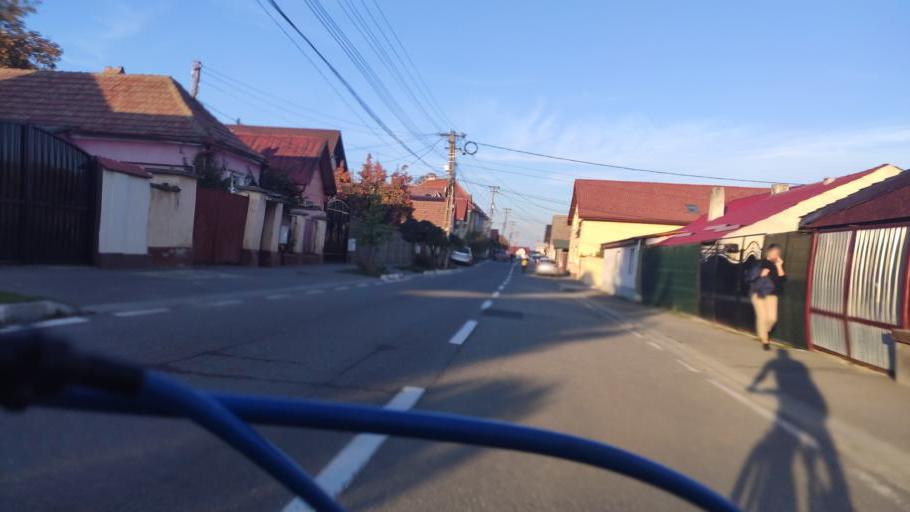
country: RO
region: Brasov
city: Codlea
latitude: 45.6927
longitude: 25.4402
